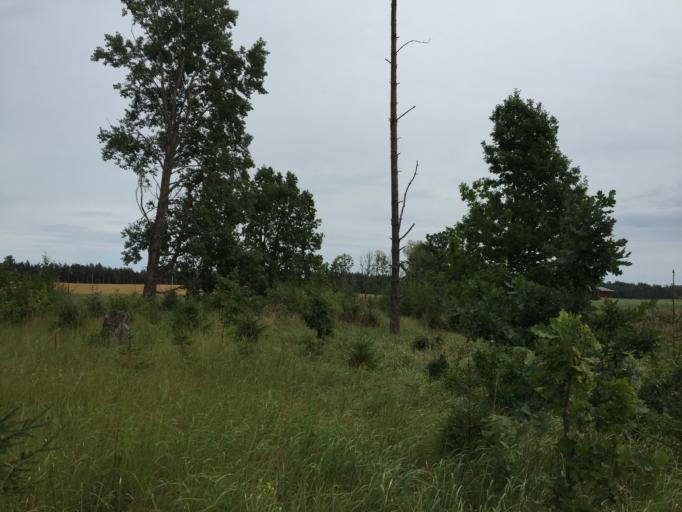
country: LV
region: Jaunpils
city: Jaunpils
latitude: 56.7298
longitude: 23.1582
